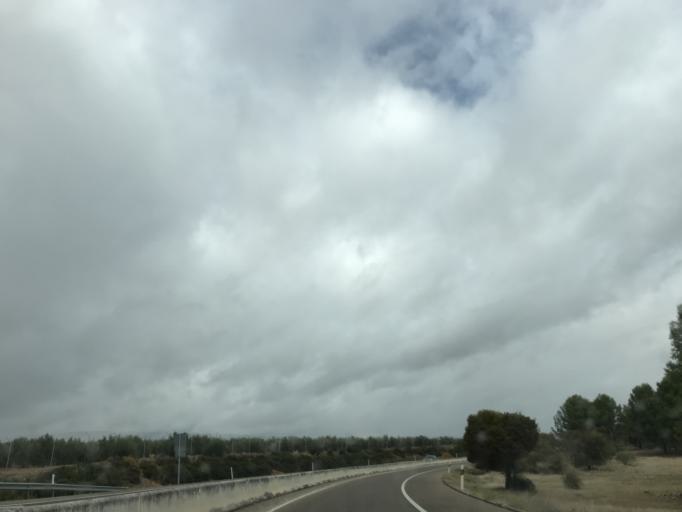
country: ES
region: Andalusia
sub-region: Provincia de Jaen
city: Bailen
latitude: 38.1228
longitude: -3.7618
